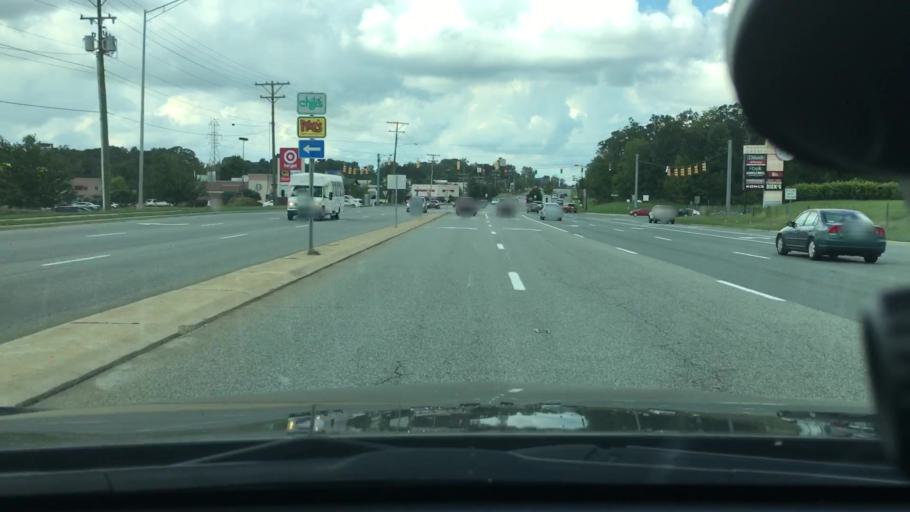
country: US
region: North Carolina
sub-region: Alamance County
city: Elon
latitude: 36.0674
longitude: -79.5186
